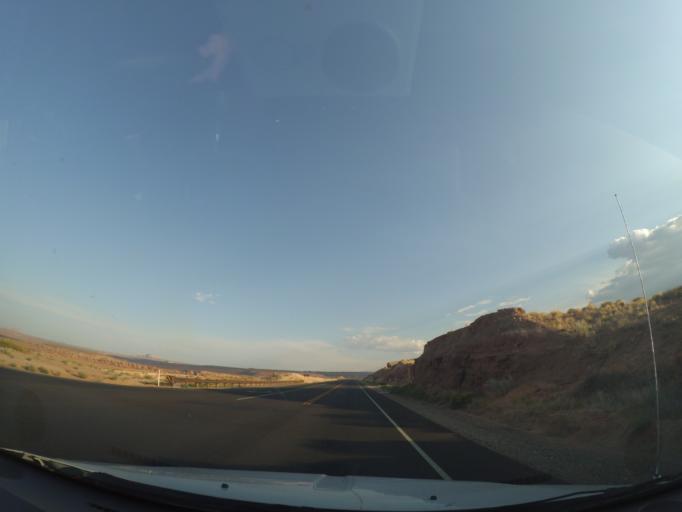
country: US
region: Arizona
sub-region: Coconino County
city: Page
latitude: 36.9713
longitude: -111.4906
